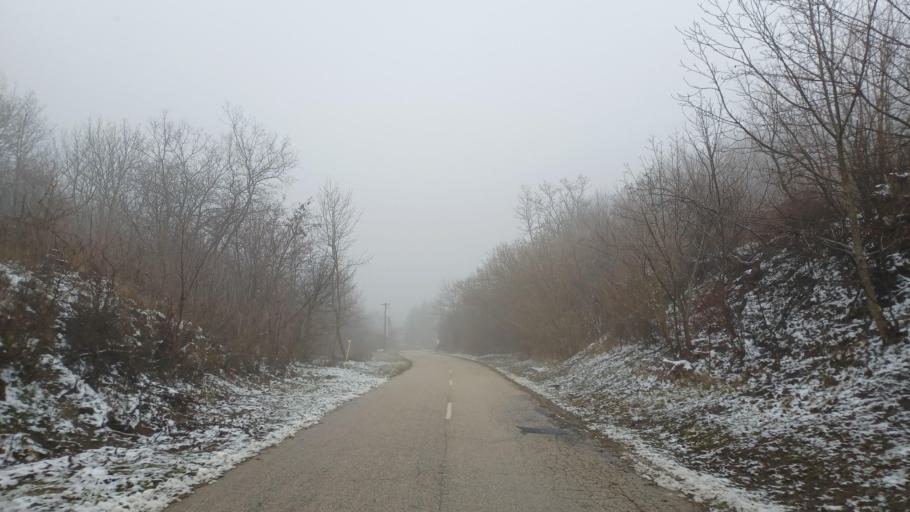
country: HU
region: Tolna
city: Gyonk
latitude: 46.6240
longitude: 18.4800
